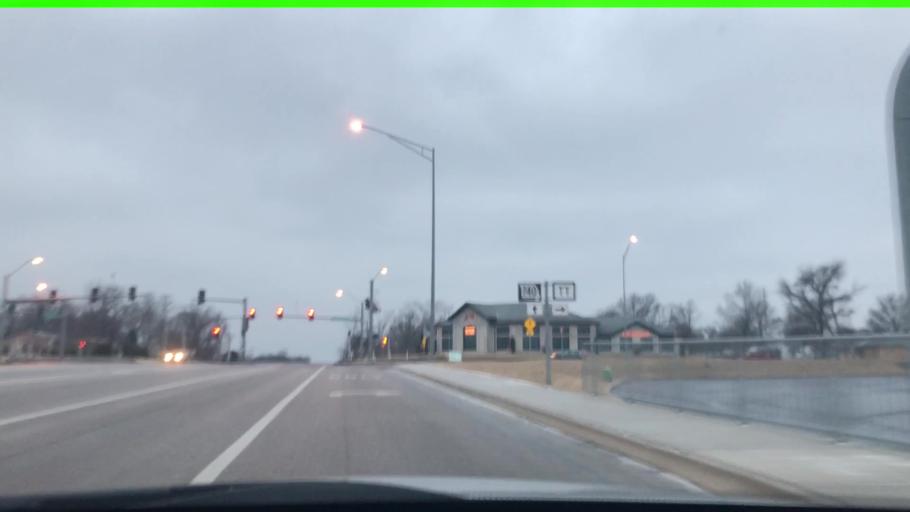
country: US
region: Missouri
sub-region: Boone County
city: Columbia
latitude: 38.9546
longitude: -92.3717
